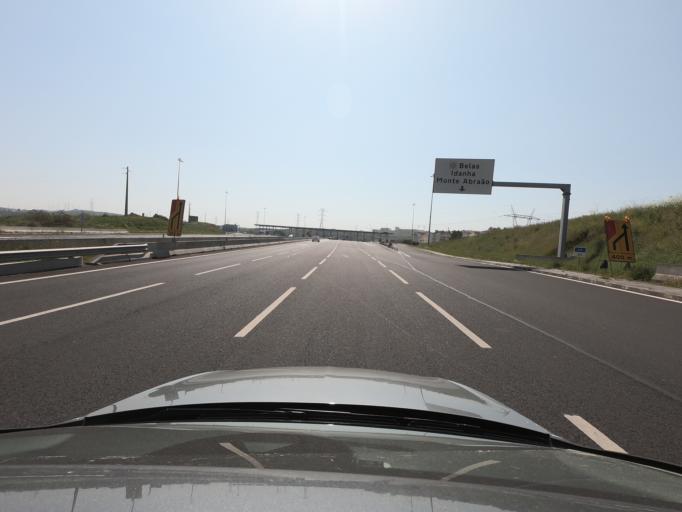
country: PT
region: Lisbon
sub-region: Sintra
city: Belas
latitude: 38.7720
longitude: -9.2776
